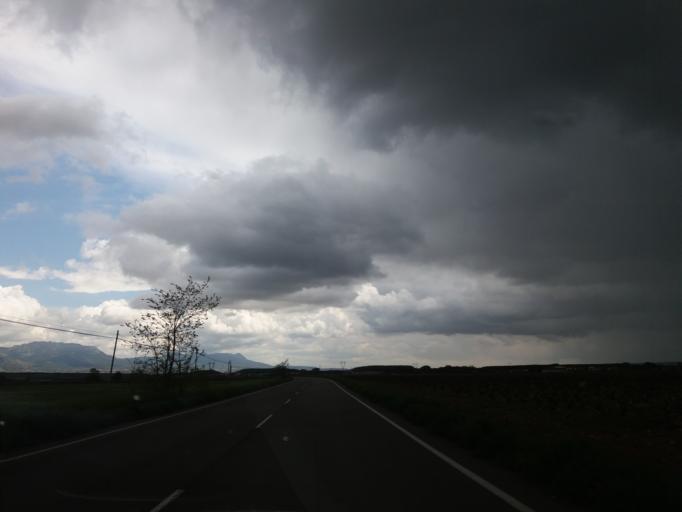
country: ES
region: La Rioja
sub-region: Provincia de La Rioja
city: Cihuri
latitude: 42.5737
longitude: -2.9321
